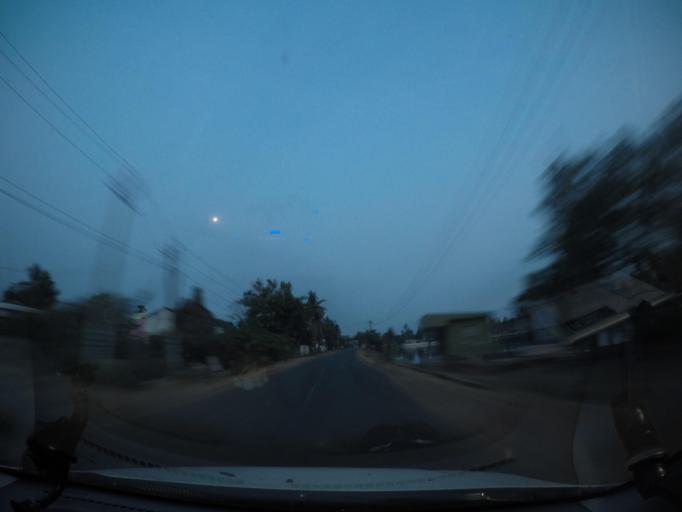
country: IN
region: Andhra Pradesh
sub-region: West Godavari
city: Tadepallegudem
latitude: 16.7823
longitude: 81.4238
